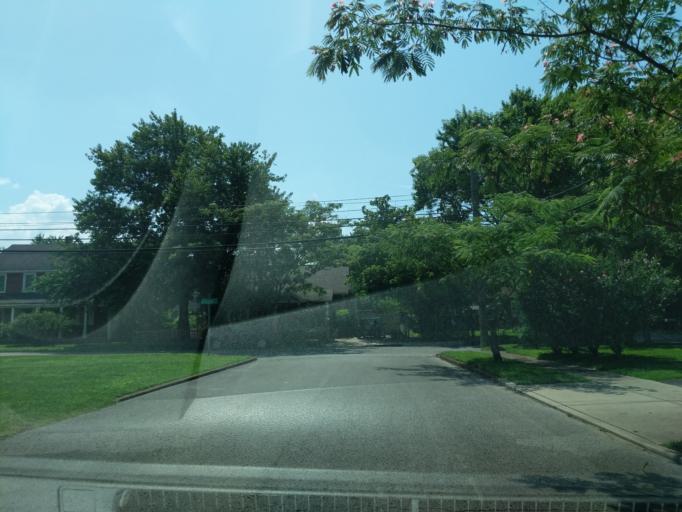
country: US
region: Tennessee
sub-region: Davidson County
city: Lakewood
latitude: 36.2598
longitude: -86.6481
